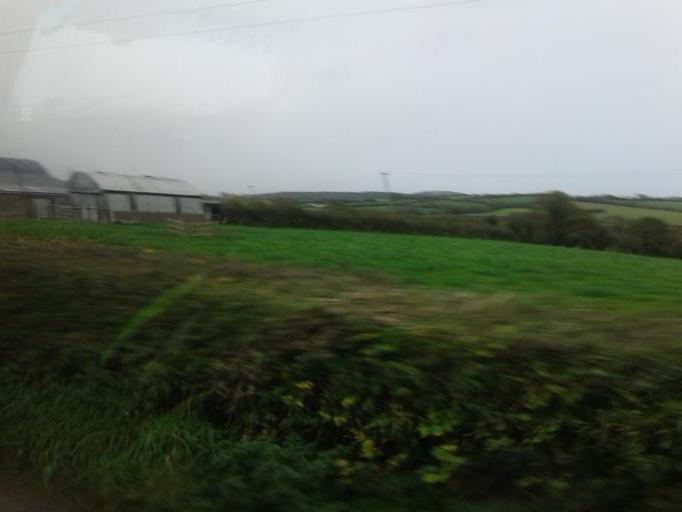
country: IE
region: Leinster
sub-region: Uibh Fhaili
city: Birr
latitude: 52.9743
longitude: -7.9820
